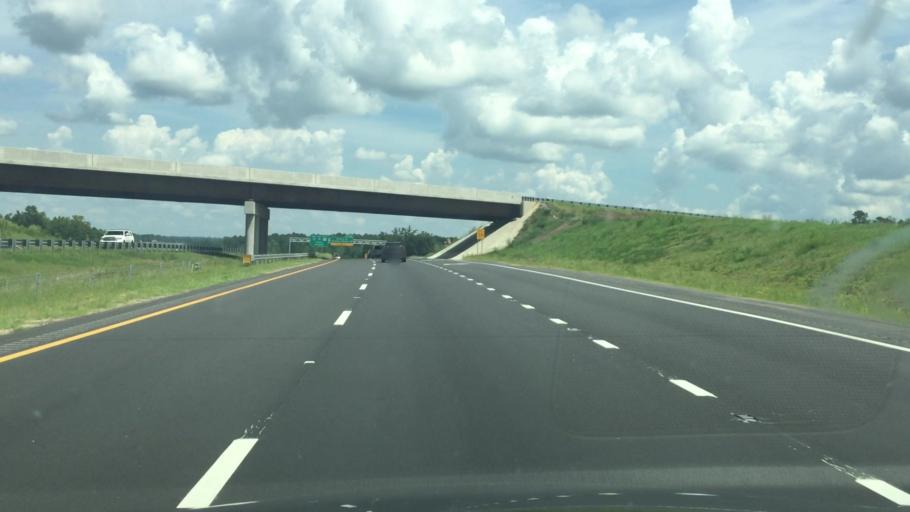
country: US
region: North Carolina
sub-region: Richmond County
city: Ellerbe
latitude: 35.0107
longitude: -79.7710
